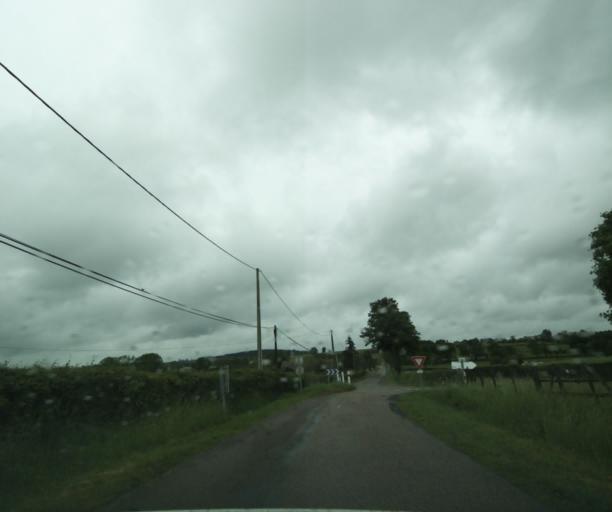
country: FR
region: Bourgogne
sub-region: Departement de Saone-et-Loire
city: Charolles
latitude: 46.4663
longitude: 4.4369
